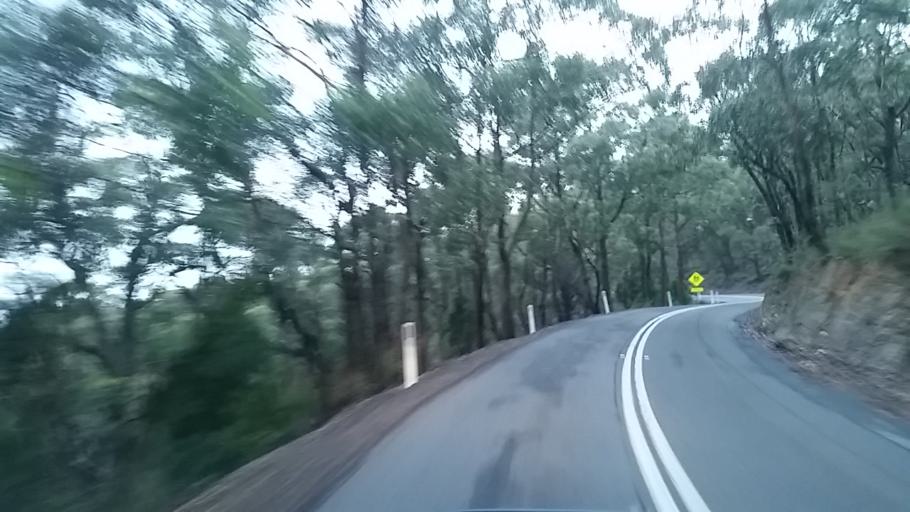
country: AU
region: South Australia
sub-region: Adelaide Hills
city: Crafers
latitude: -34.9751
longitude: 138.7076
